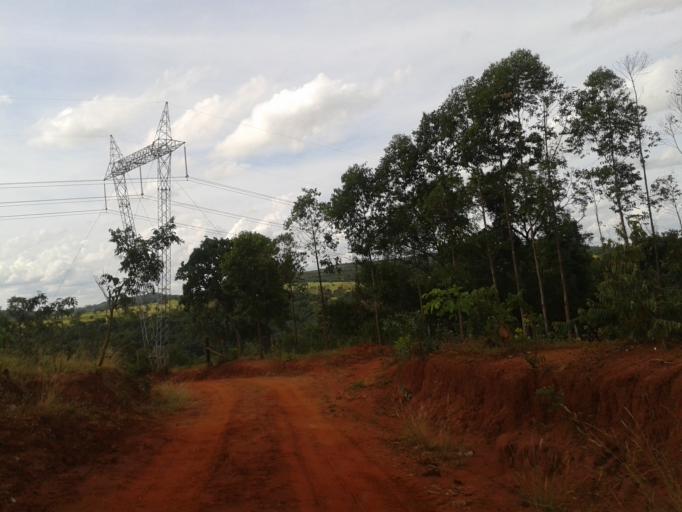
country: BR
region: Minas Gerais
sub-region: Campina Verde
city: Campina Verde
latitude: -19.4377
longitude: -49.6169
